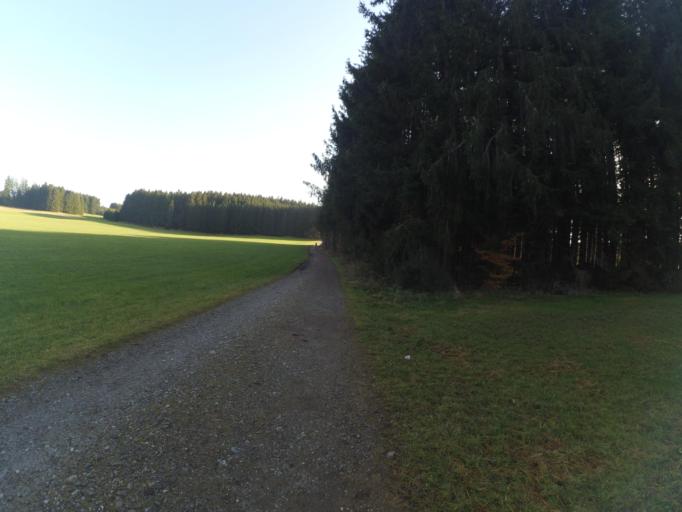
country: DE
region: Bavaria
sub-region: Swabia
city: Ruderatshofen
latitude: 47.8067
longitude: 10.5611
